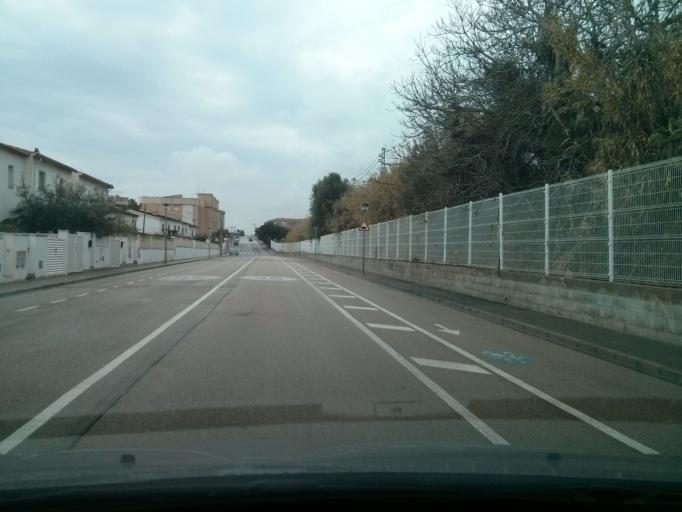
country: ES
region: Catalonia
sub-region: Provincia de Tarragona
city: El Vendrell
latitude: 41.1867
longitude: 1.5326
